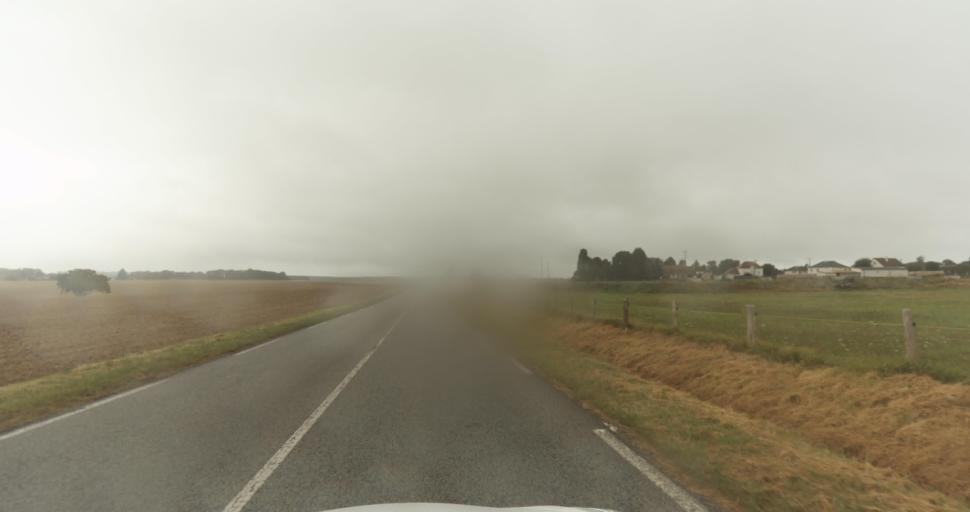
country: FR
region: Haute-Normandie
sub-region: Departement de l'Eure
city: Heudreville-sur-Eure
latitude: 49.1118
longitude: 1.1741
